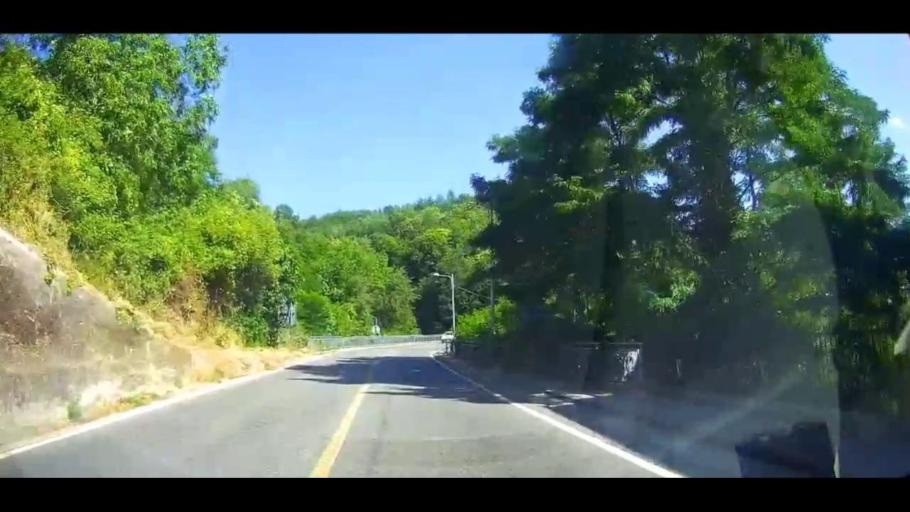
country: IT
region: Calabria
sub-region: Provincia di Cosenza
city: Celico
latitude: 39.3103
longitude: 16.3395
